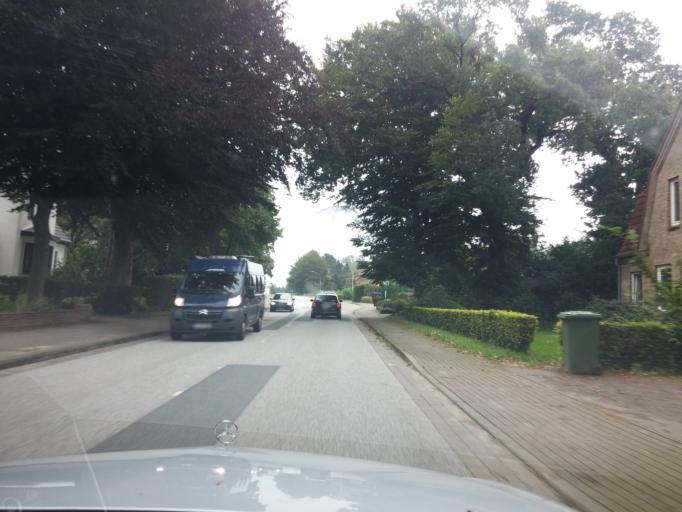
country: DE
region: Schleswig-Holstein
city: Oster-Ohrstedt
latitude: 54.5145
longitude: 9.2279
